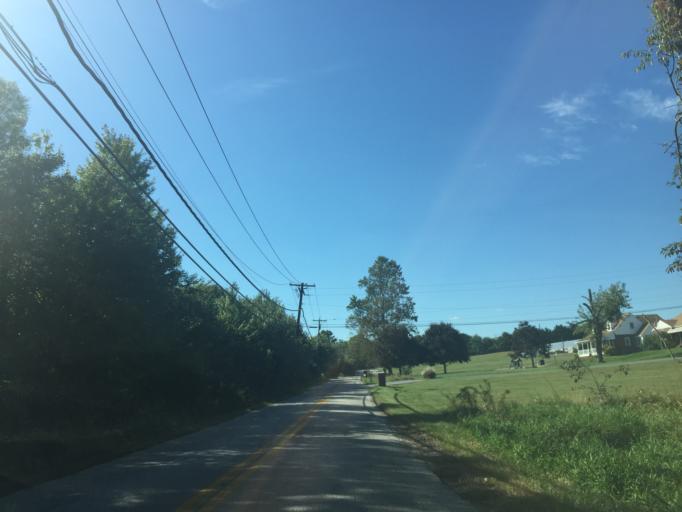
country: US
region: Maryland
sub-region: Baltimore County
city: Overlea
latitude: 39.3747
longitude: -76.4915
